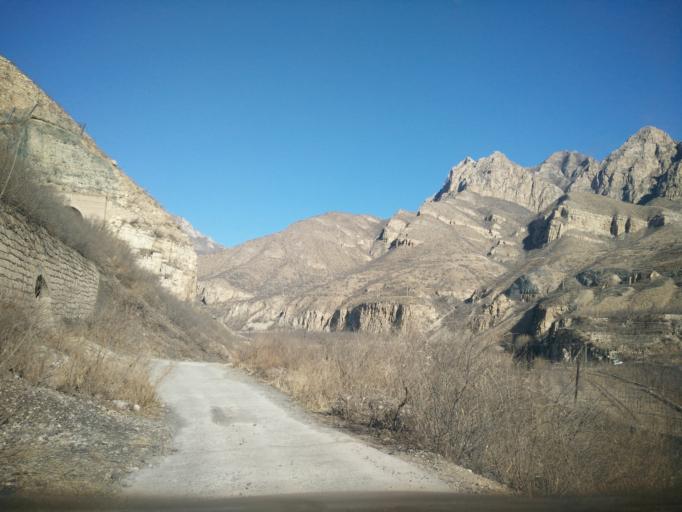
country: CN
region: Beijing
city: Zhaitang
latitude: 40.1617
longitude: 115.6686
